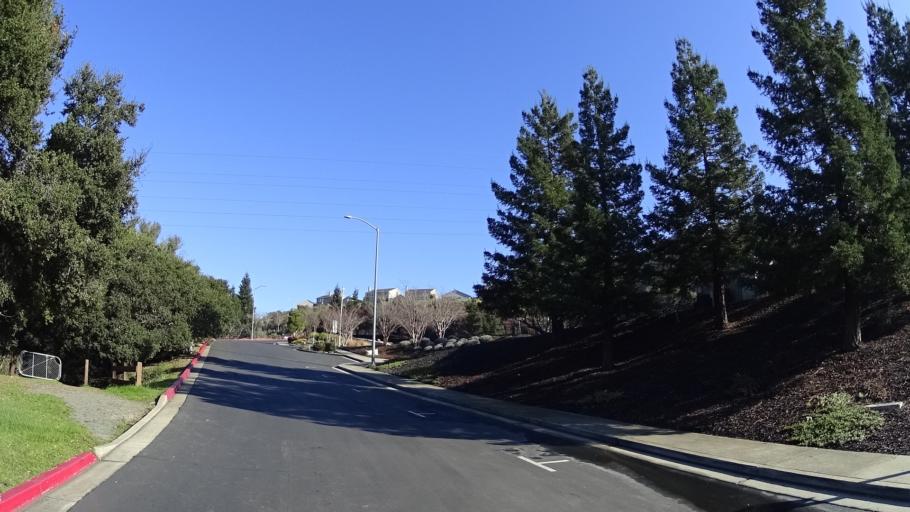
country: US
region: California
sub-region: Alameda County
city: Fairview
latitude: 37.6870
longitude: -122.0427
